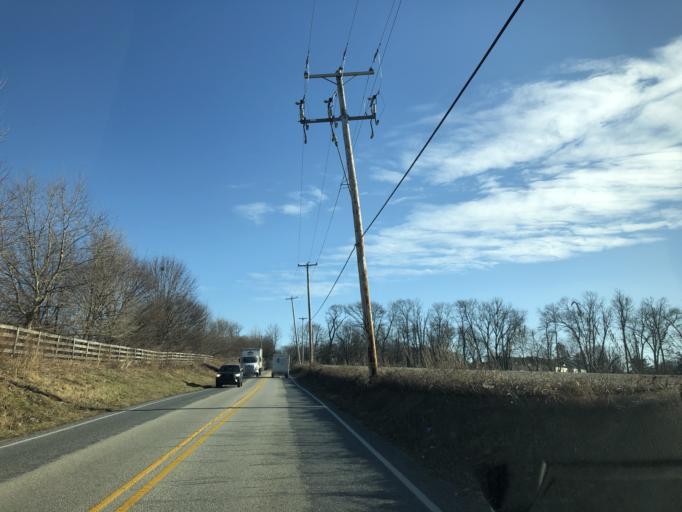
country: US
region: Pennsylvania
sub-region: Chester County
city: Toughkenamon
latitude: 39.8523
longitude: -75.7699
